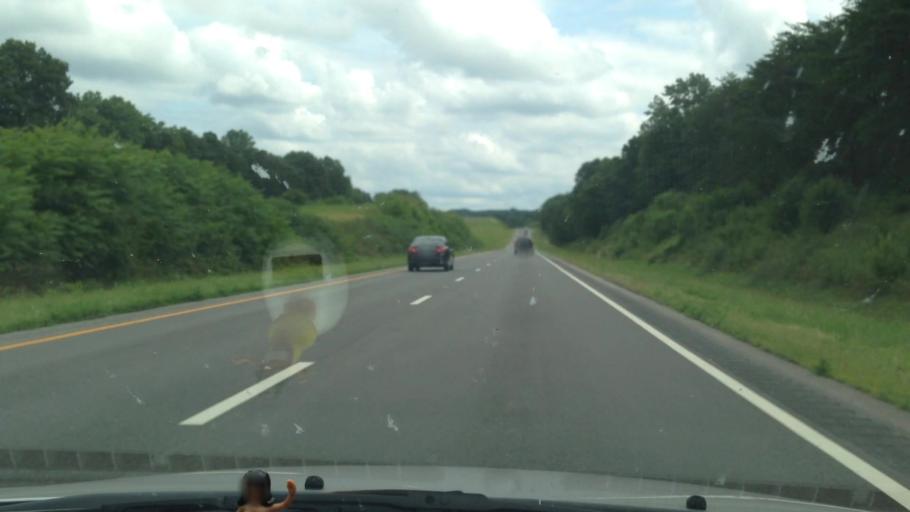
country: US
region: Virginia
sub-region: Pittsylvania County
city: Gretna
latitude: 36.9685
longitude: -79.3635
